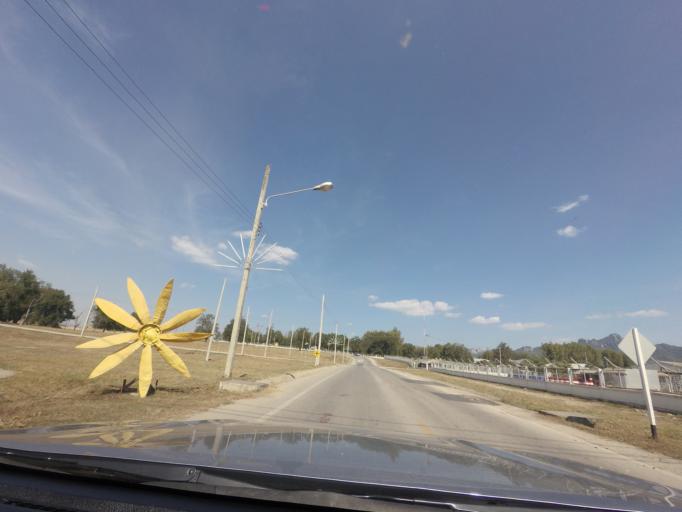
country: TH
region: Lampang
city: Mae Mo
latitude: 18.2990
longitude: 99.7322
